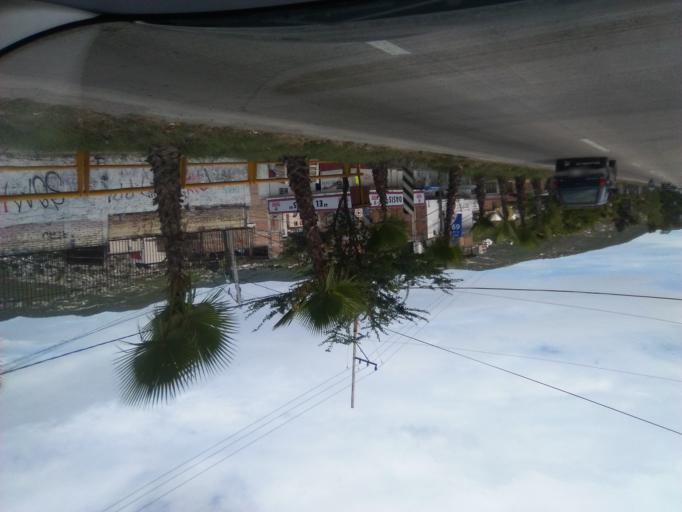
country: MX
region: Guerrero
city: Chilpancingo de los Bravos
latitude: 17.5550
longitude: -99.5093
